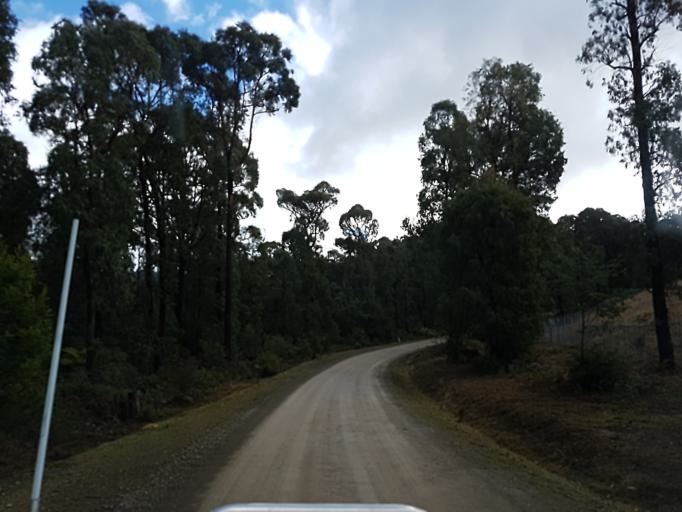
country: AU
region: Victoria
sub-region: Yarra Ranges
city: Millgrove
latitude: -37.5235
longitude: 145.7408
